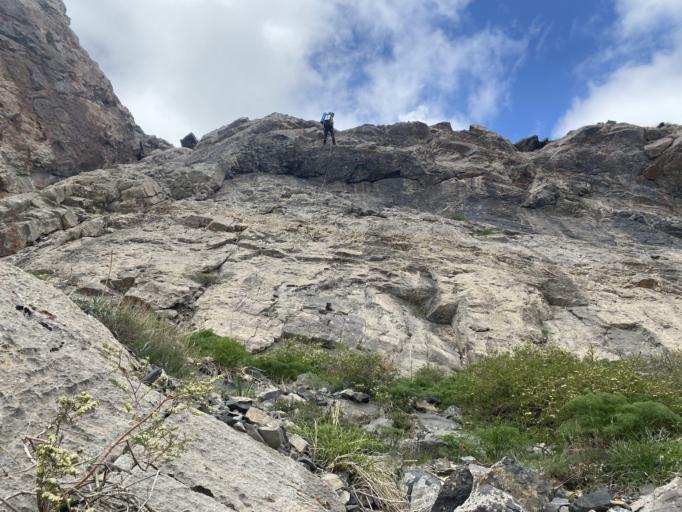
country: KZ
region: Ongtustik Qazaqstan
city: Ashchysay
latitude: 43.6463
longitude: 68.8993
